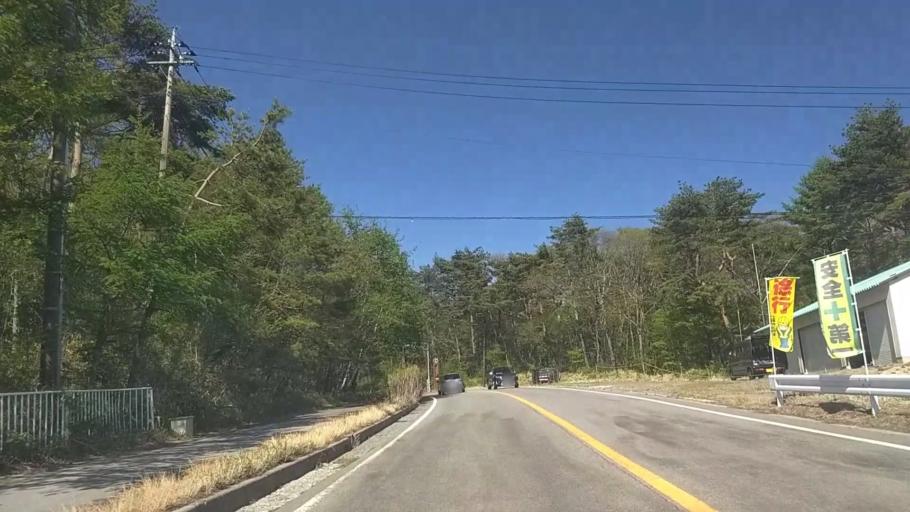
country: JP
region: Yamanashi
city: Nirasaki
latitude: 35.9258
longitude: 138.4402
